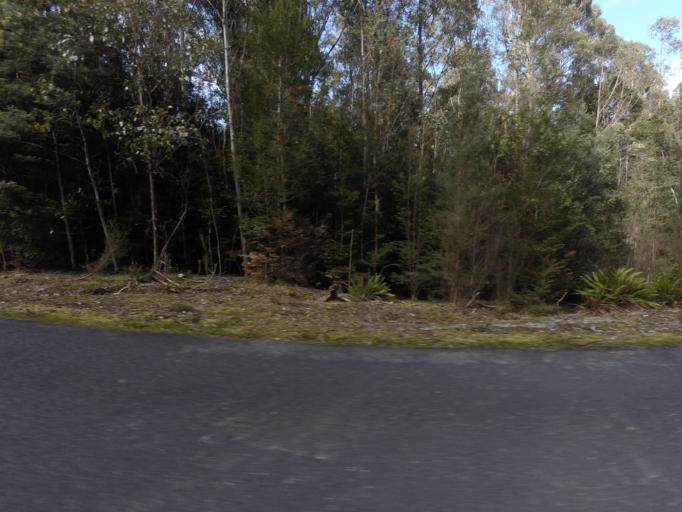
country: AU
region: Tasmania
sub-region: Huon Valley
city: Geeveston
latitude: -42.8188
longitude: 146.3326
